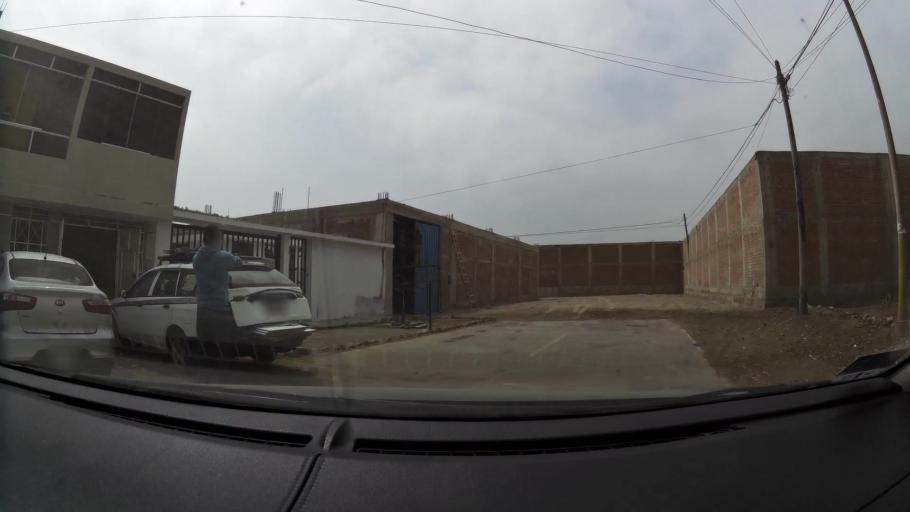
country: PE
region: Lima
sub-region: Lima
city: Santa Rosa
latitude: -11.7885
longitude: -77.1527
